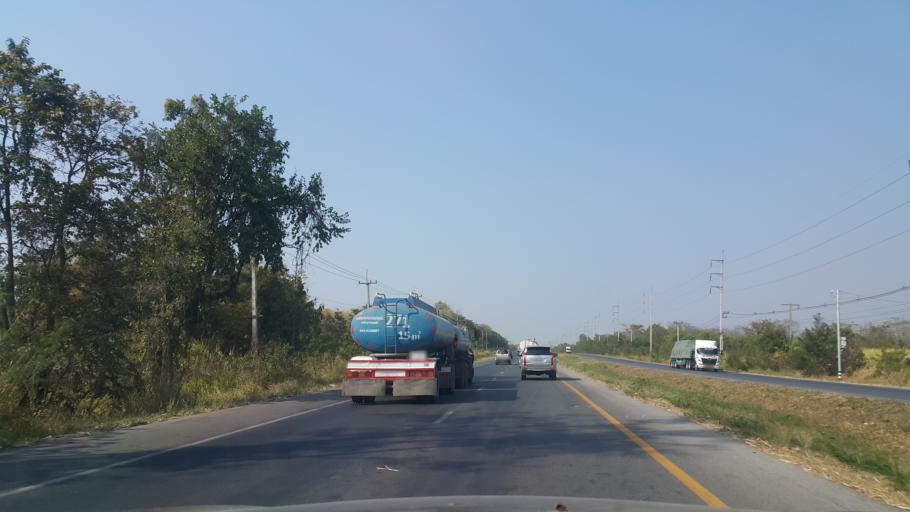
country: TH
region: Chaiyaphum
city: Phu Khiao
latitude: 16.4424
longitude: 102.1253
